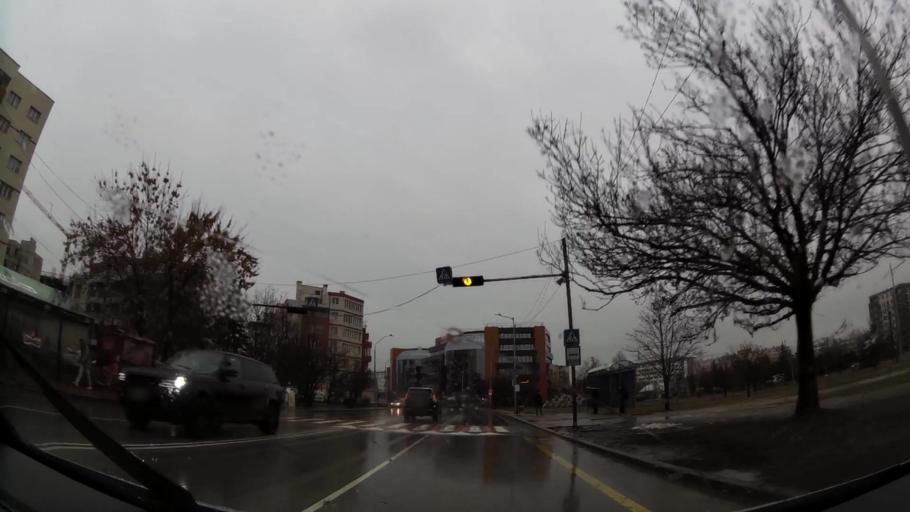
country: BG
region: Sofia-Capital
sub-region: Stolichna Obshtina
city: Sofia
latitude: 42.6559
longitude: 23.3495
